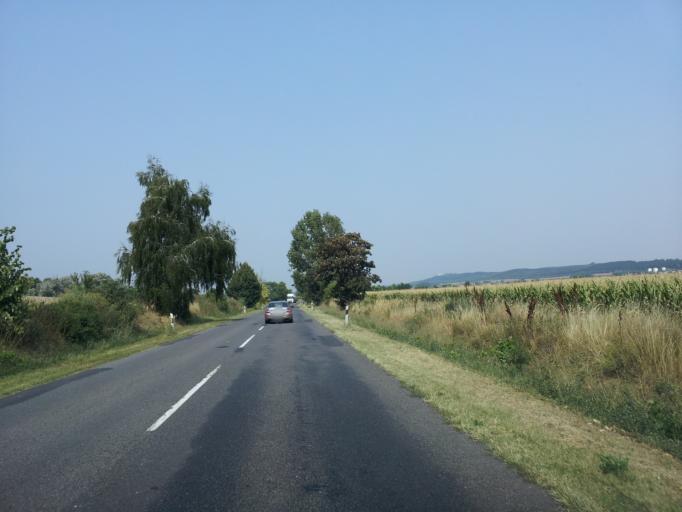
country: HU
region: Gyor-Moson-Sopron
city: Pannonhalma
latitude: 47.4886
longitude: 17.7826
